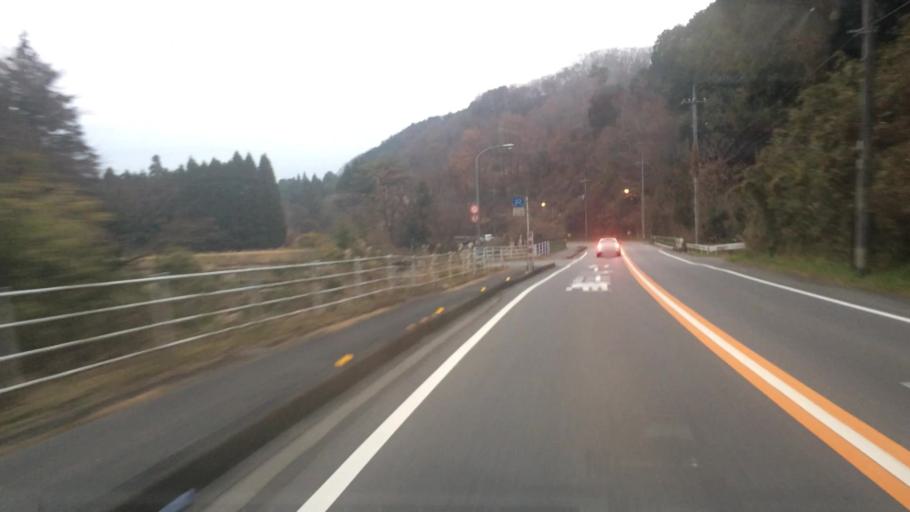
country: JP
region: Tochigi
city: Utsunomiya-shi
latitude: 36.6432
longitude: 139.8038
